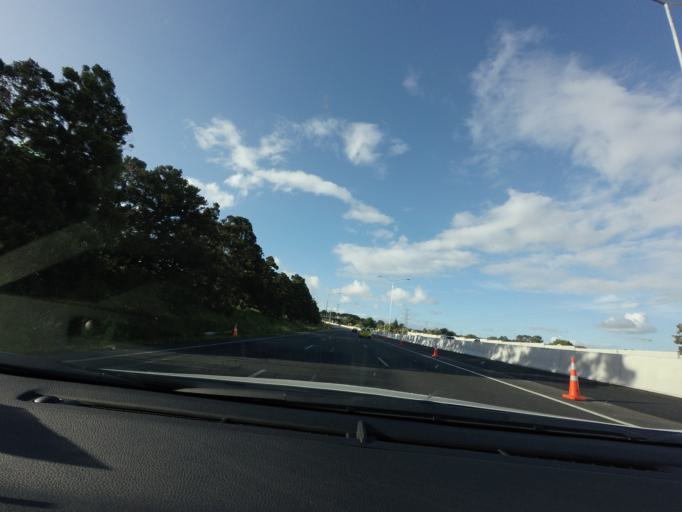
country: NZ
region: Auckland
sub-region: Auckland
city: Takanini
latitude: -37.0228
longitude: 174.9098
